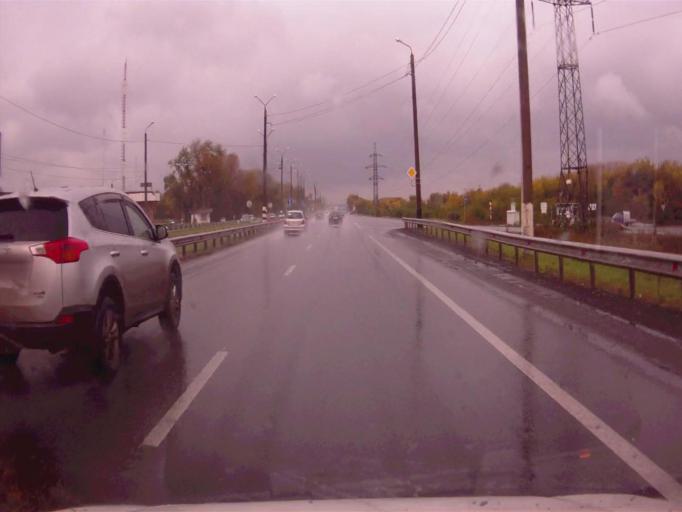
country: RU
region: Chelyabinsk
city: Dolgoderevenskoye
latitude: 55.2546
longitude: 61.3533
